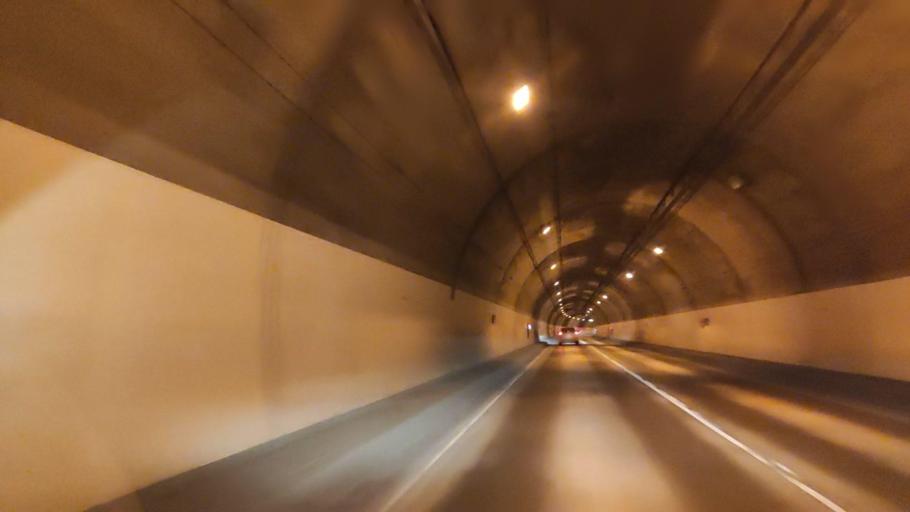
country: JP
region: Hokkaido
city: Ishikari
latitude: 43.4575
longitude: 141.4074
